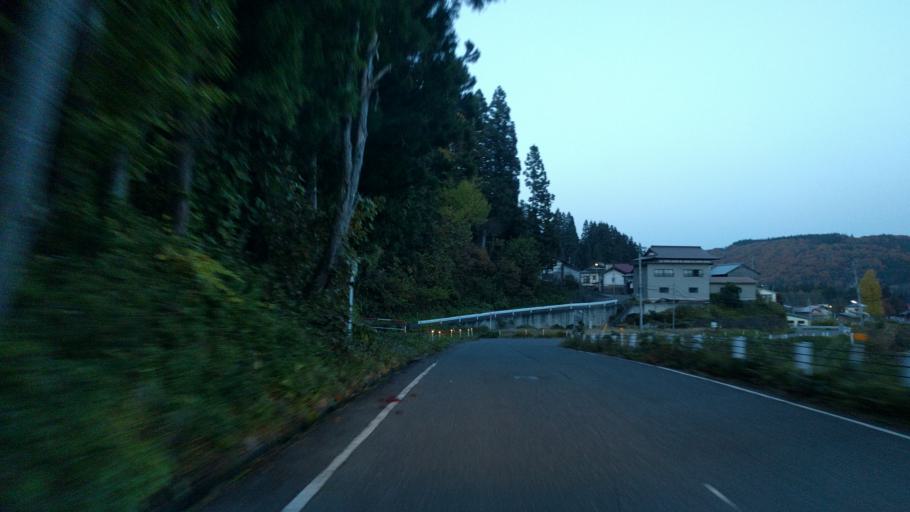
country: JP
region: Fukushima
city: Kitakata
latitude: 37.5288
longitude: 139.7141
